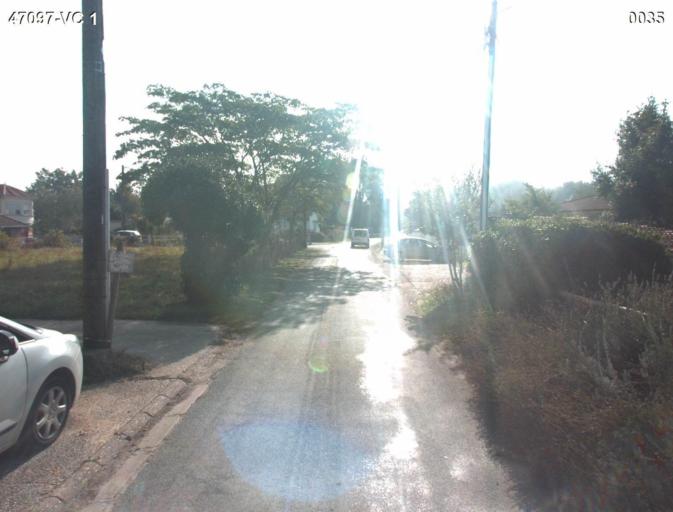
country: FR
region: Aquitaine
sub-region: Departement du Lot-et-Garonne
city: Vianne
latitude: 44.2209
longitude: 0.3465
